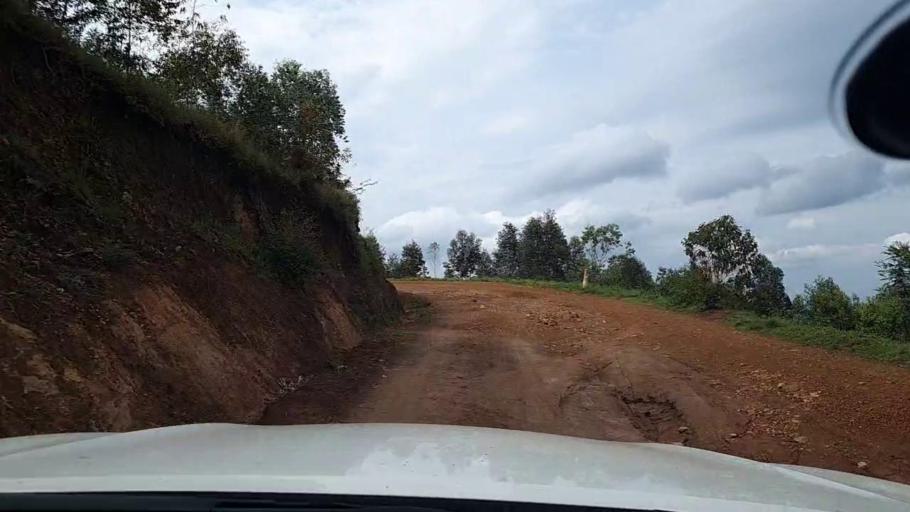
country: RW
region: Western Province
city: Kibuye
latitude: -2.1294
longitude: 29.3742
